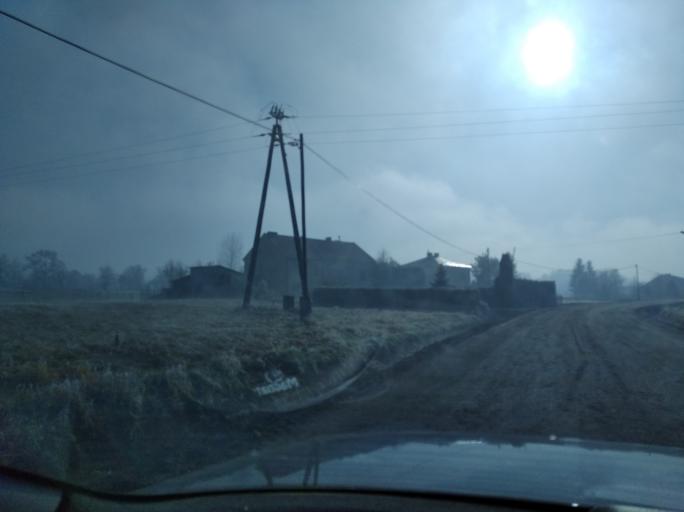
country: PL
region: Subcarpathian Voivodeship
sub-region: Powiat strzyzowski
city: Wisniowa
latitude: 49.8719
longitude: 21.7059
